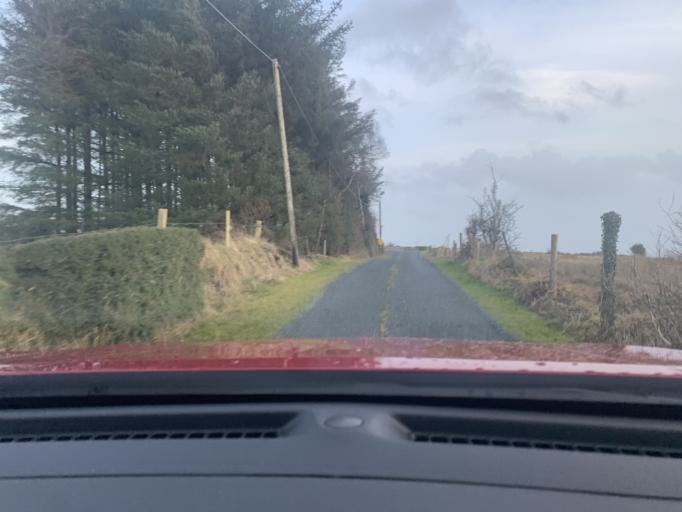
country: IE
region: Connaught
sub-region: Roscommon
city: Ballaghaderreen
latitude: 53.9490
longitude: -8.5125
